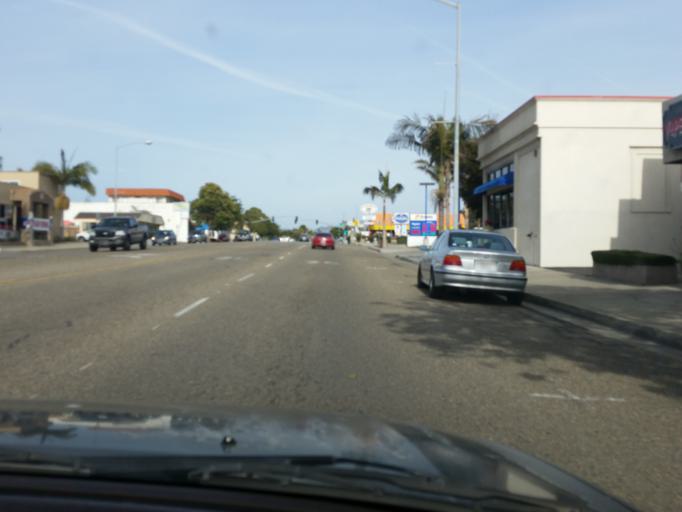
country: US
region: California
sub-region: San Luis Obispo County
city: Grover Beach
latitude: 35.1216
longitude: -120.6237
